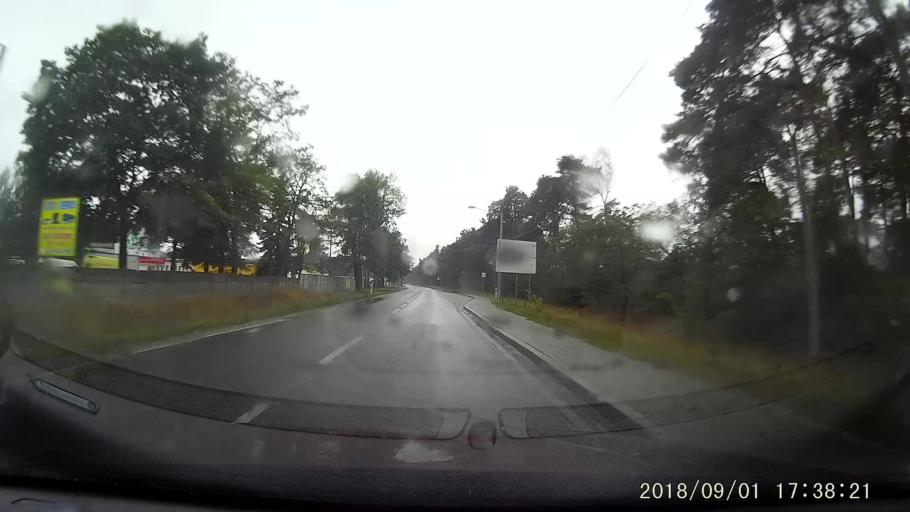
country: PL
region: Lubusz
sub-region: Powiat zaganski
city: Zagan
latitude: 51.6018
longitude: 15.2954
